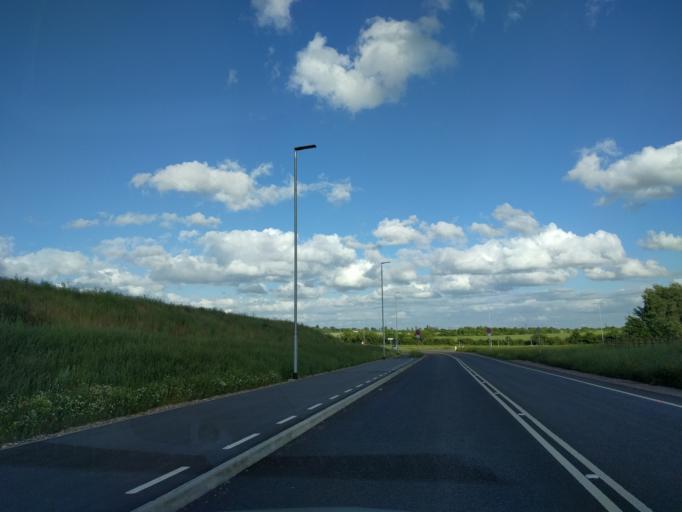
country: GB
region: England
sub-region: Nottinghamshire
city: Newark on Trent
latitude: 53.0458
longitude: -0.7921
